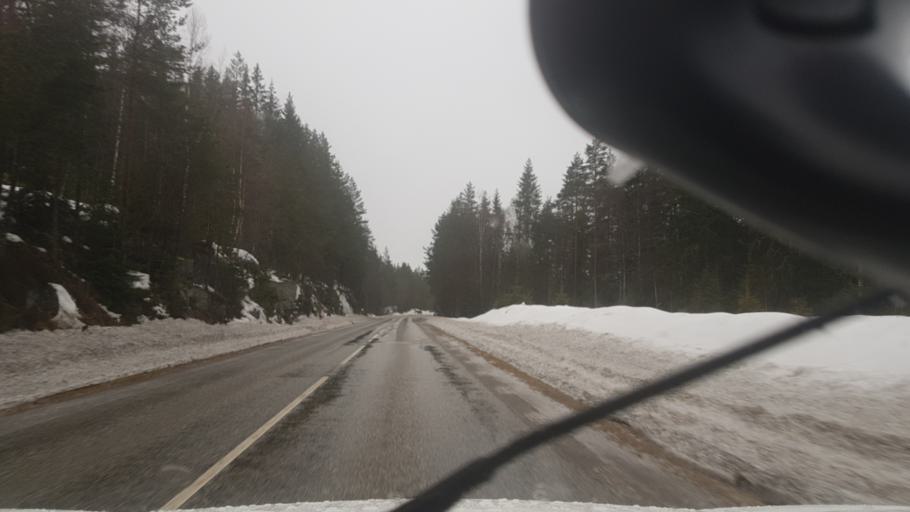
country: SE
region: Vaermland
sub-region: Eda Kommun
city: Amotfors
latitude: 59.5917
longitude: 12.2965
